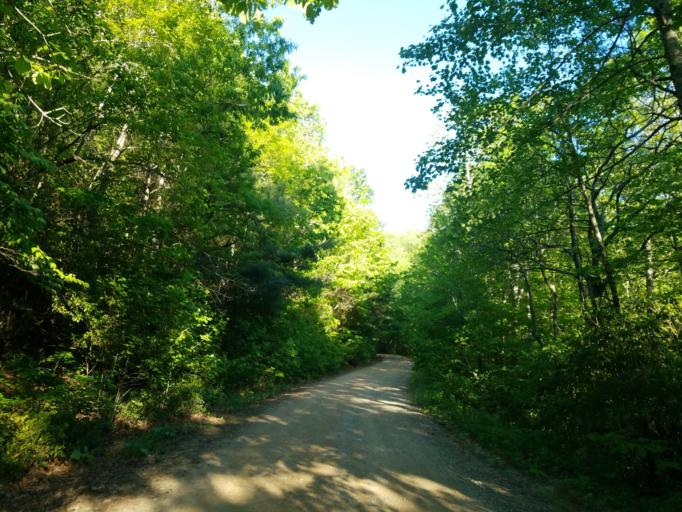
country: US
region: Georgia
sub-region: Lumpkin County
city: Dahlonega
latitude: 34.6687
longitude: -84.1294
